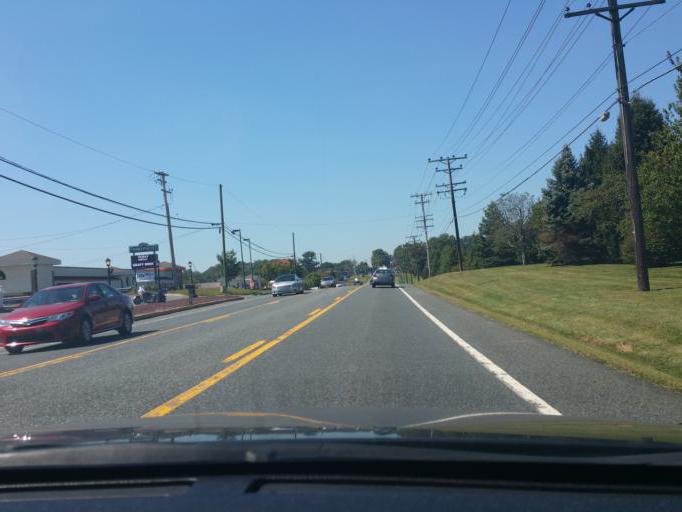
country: US
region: Maryland
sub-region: Harford County
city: South Bel Air
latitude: 39.5552
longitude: -76.2801
